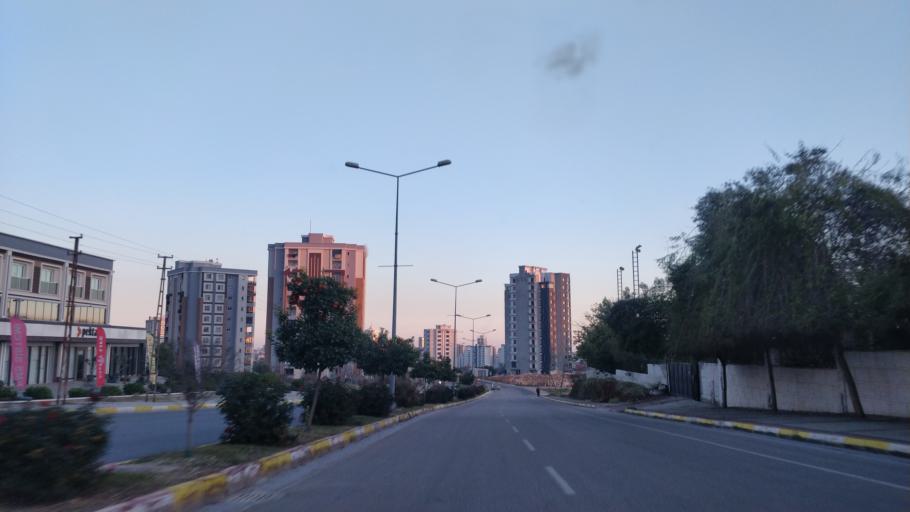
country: TR
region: Mersin
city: Mercin
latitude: 36.8017
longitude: 34.5716
